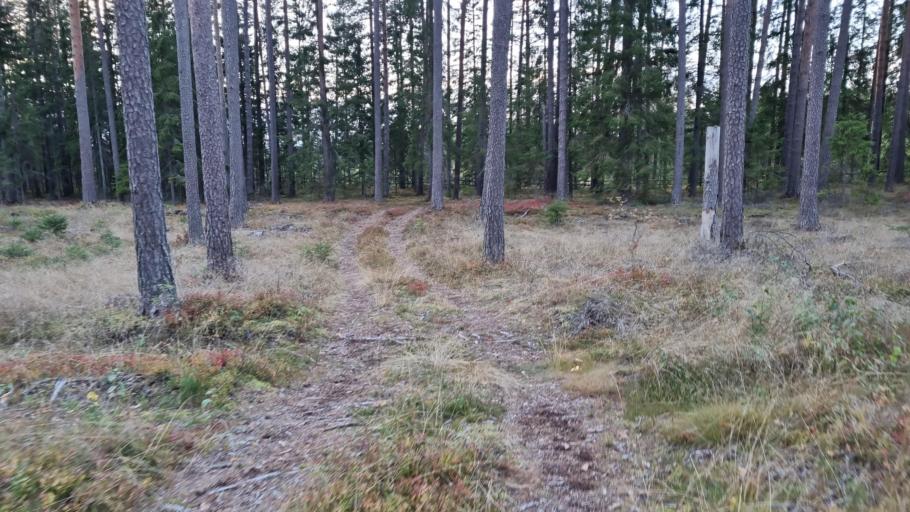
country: LV
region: Mazsalaca
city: Mazsalaca
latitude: 57.8925
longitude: 25.0131
